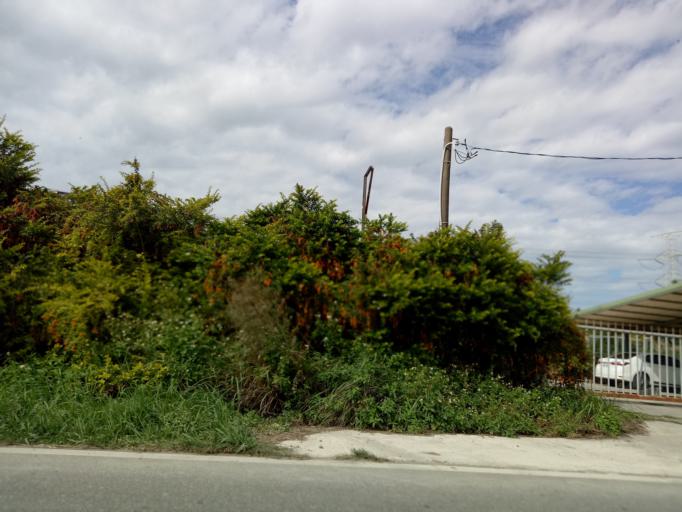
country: TW
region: Taiwan
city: Daxi
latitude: 24.8980
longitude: 121.2894
